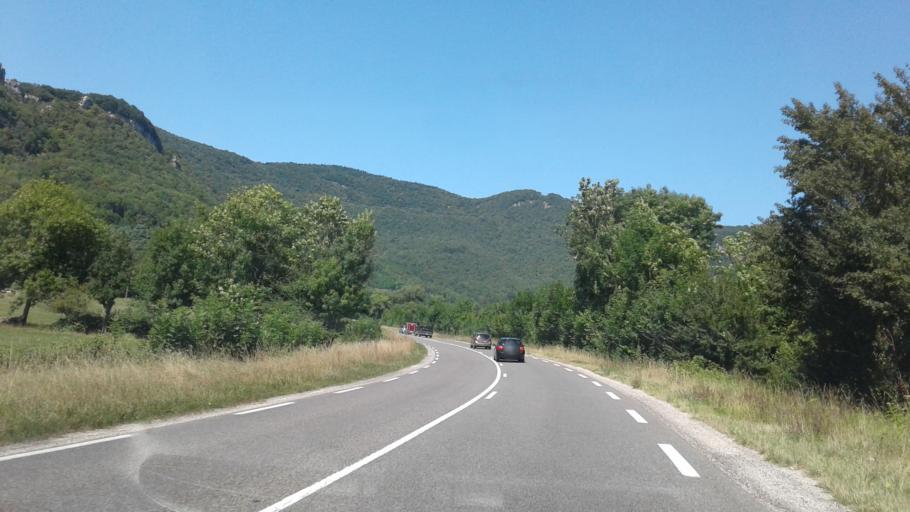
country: FR
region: Rhone-Alpes
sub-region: Departement de l'Ain
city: Saint-Rambert-en-Bugey
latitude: 45.9205
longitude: 5.4057
